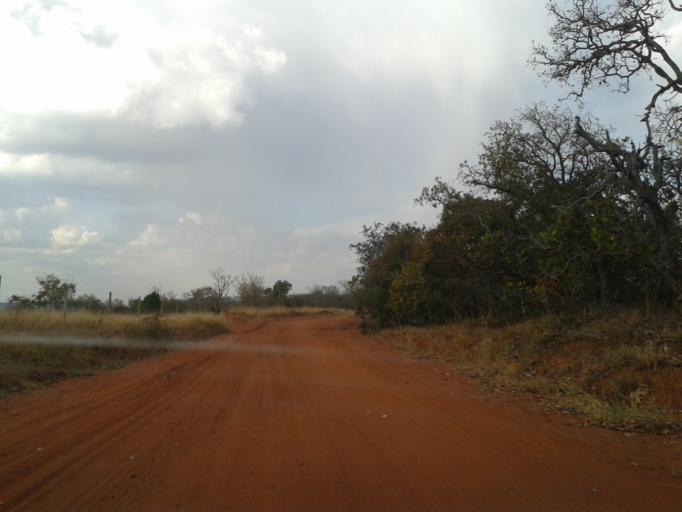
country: BR
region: Minas Gerais
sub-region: Santa Vitoria
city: Santa Vitoria
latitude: -19.1866
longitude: -49.8645
